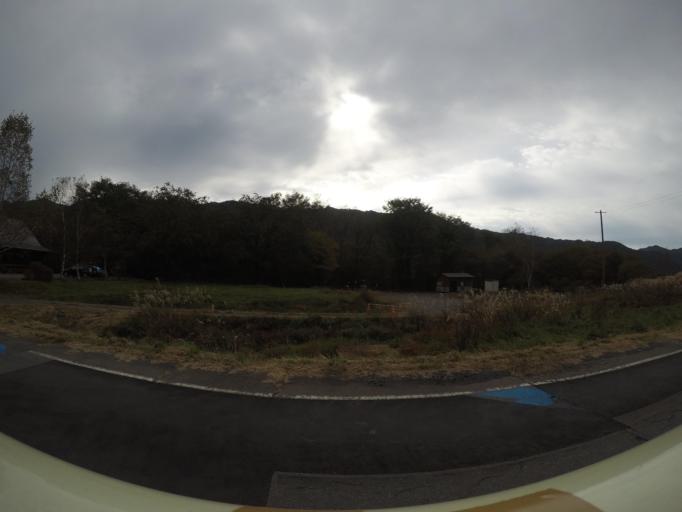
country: JP
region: Nagano
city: Ina
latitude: 35.9490
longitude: 137.6417
